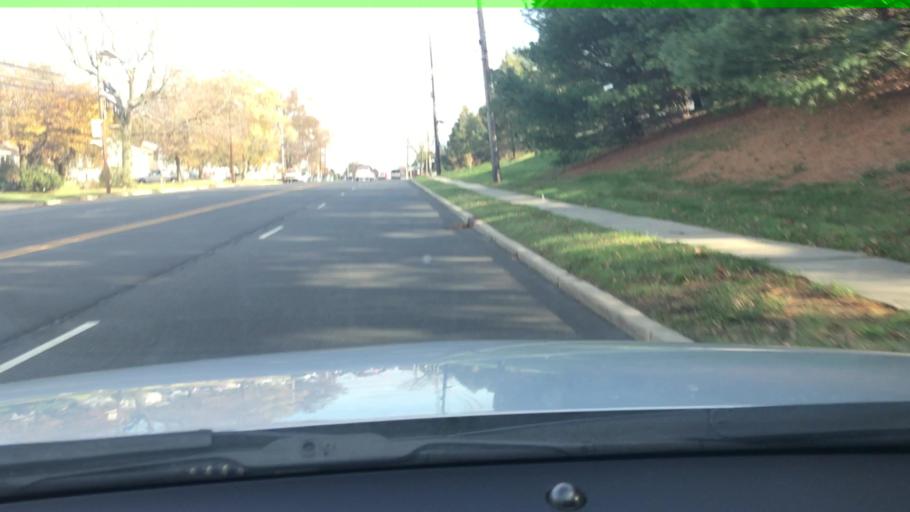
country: US
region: New Jersey
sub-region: Mercer County
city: Mercerville
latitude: 40.2203
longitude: -74.6761
